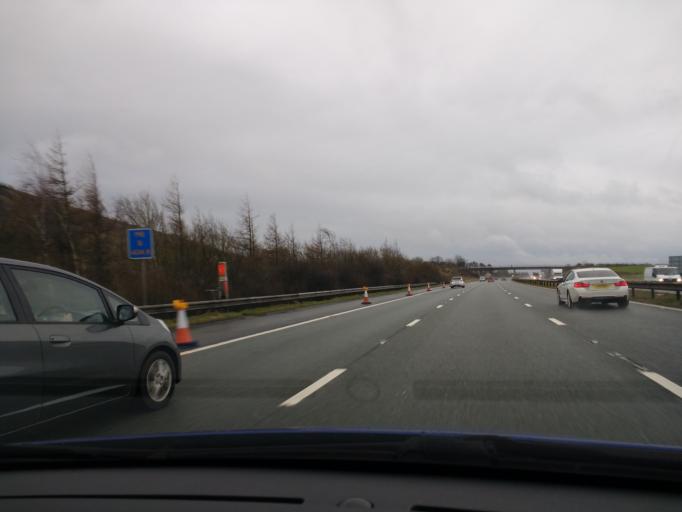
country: GB
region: England
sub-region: Cumbria
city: Milnthorpe
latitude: 54.2231
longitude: -2.7207
